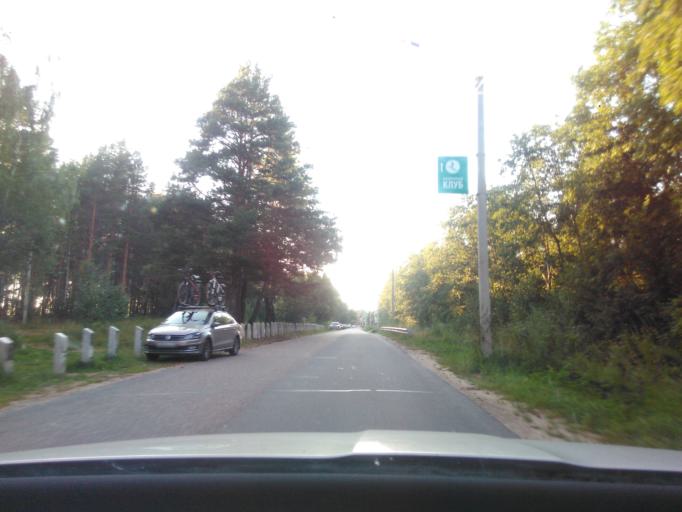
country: RU
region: Tverskaya
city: Konakovo
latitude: 56.7492
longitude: 36.7613
